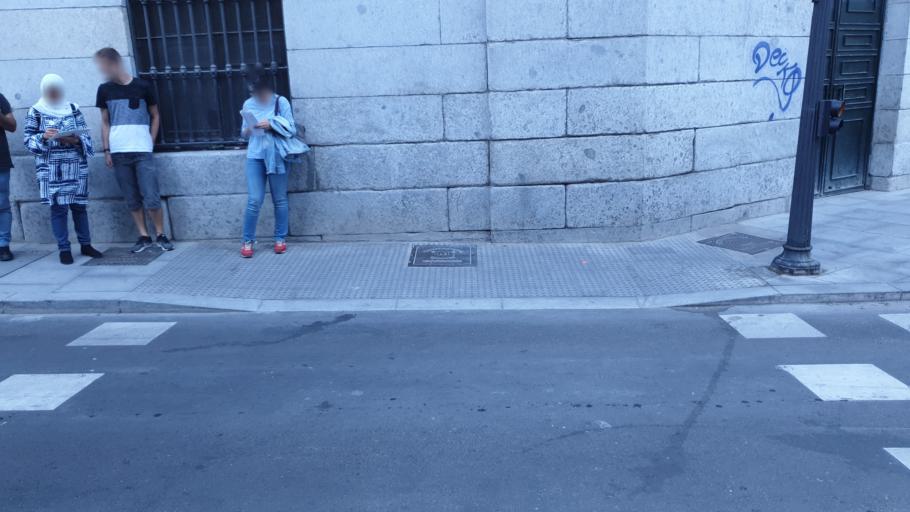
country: ES
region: Madrid
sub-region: Provincia de Madrid
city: City Center
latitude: 40.4245
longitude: -3.7092
